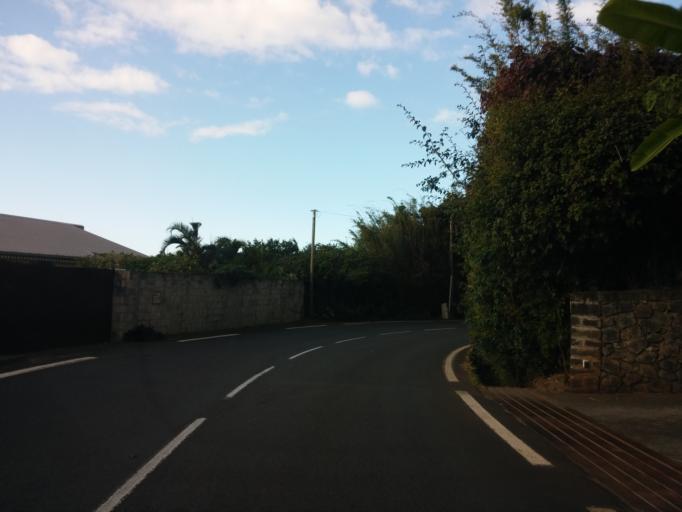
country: RE
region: Reunion
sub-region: Reunion
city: Saint-Denis
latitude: -20.8921
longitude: 55.4187
